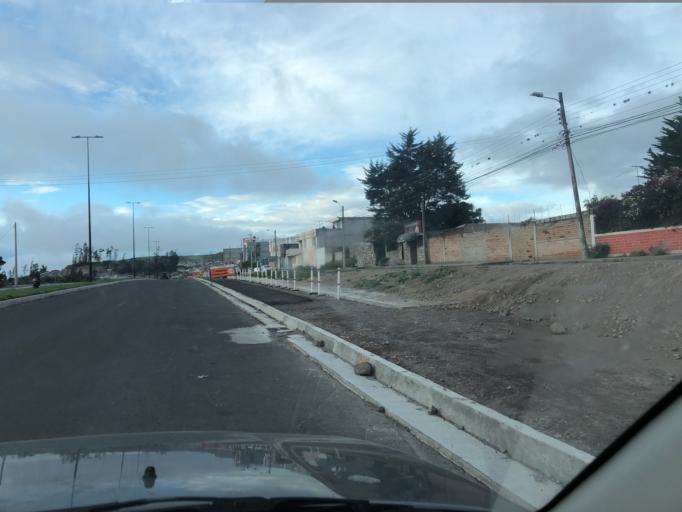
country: EC
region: Imbabura
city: Ibarra
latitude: 0.3520
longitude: -78.1407
